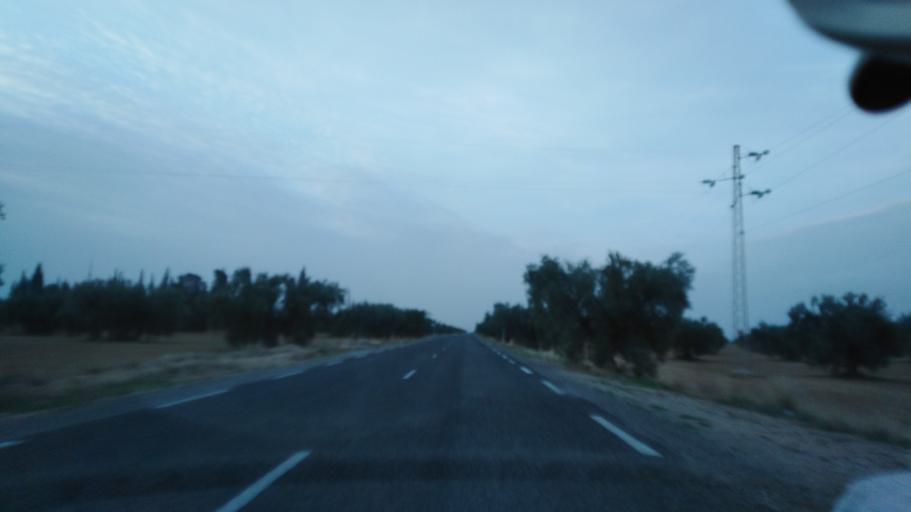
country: TN
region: Safaqis
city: Bi'r `Ali Bin Khalifah
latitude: 34.9113
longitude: 10.3876
